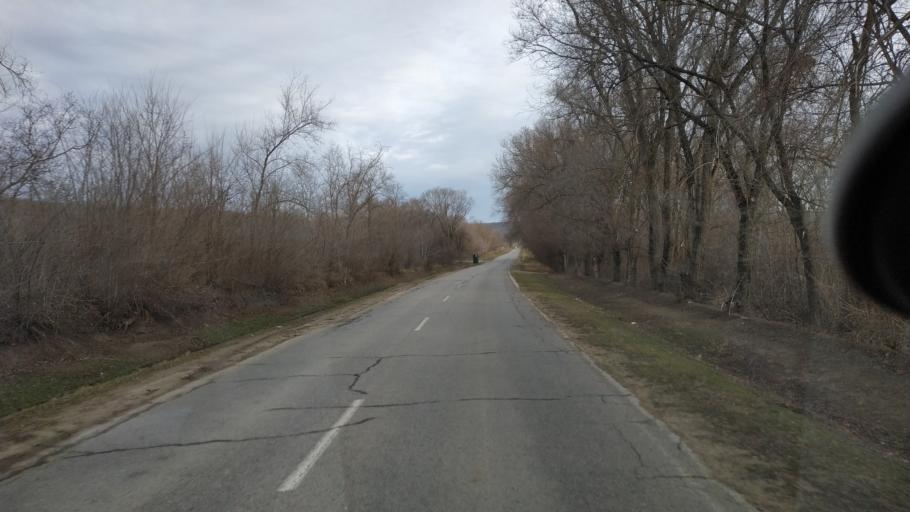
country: MD
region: Chisinau
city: Vadul lui Voda
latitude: 47.1294
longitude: 29.0624
